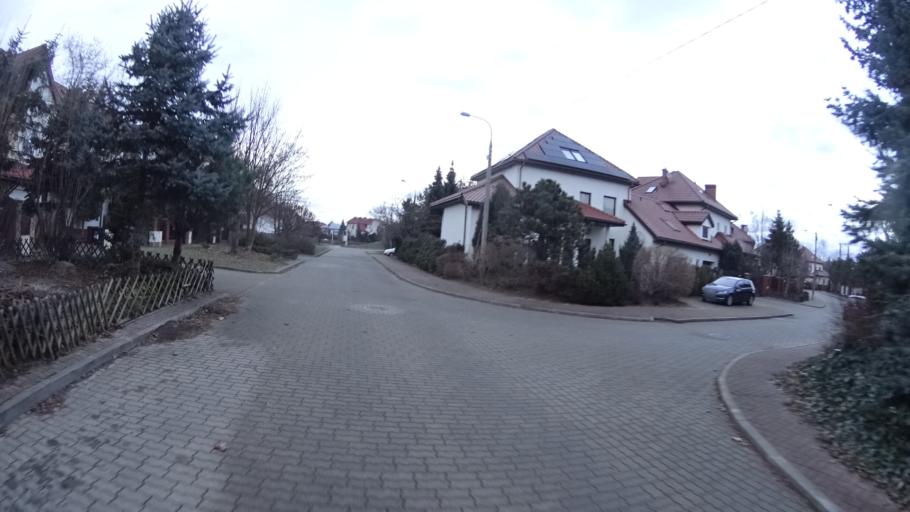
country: PL
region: Masovian Voivodeship
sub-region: Powiat pruszkowski
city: Nadarzyn
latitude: 52.1037
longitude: 20.7998
